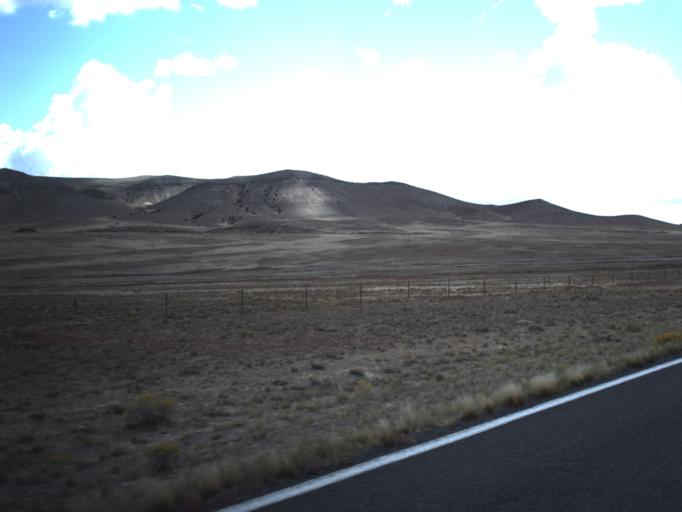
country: US
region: Utah
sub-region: Beaver County
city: Milford
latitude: 38.6419
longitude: -113.8625
